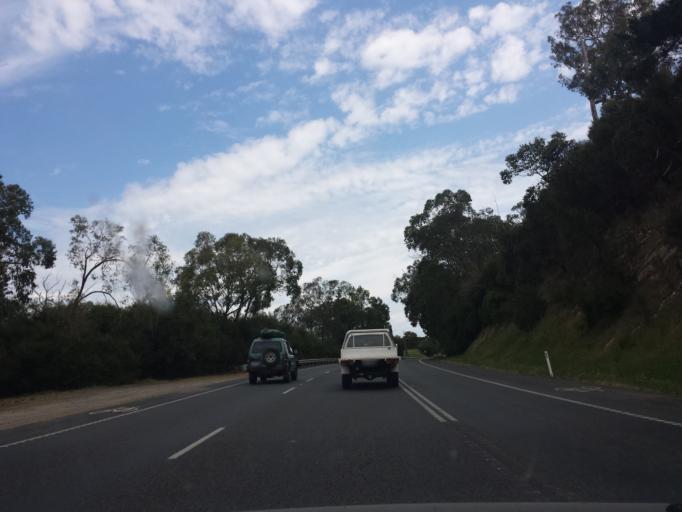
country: AU
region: Victoria
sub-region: Yarra Ranges
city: Badger Creek
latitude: -37.6822
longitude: 145.4868
